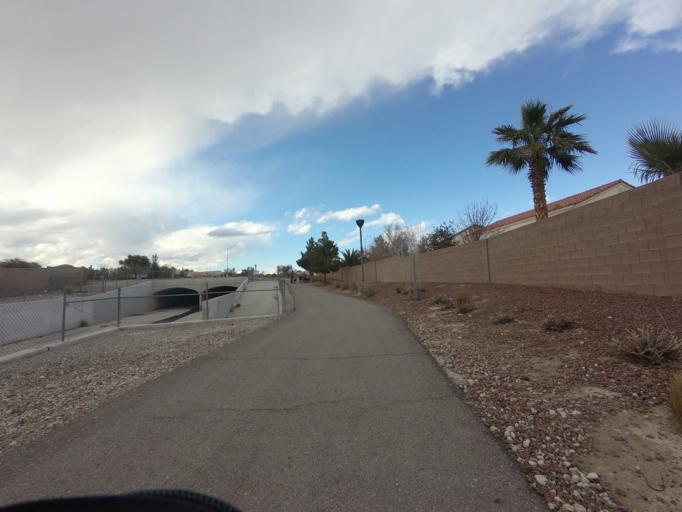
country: US
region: Nevada
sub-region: Clark County
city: North Las Vegas
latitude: 36.2646
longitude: -115.1928
